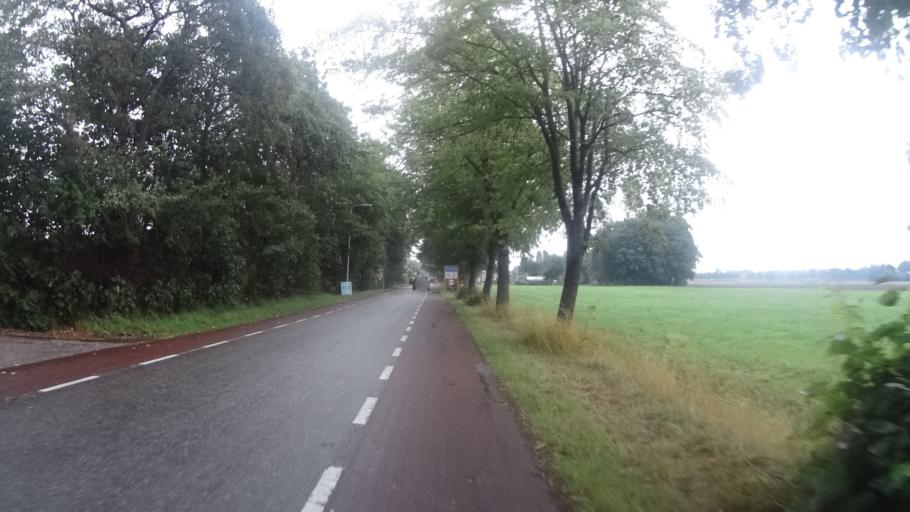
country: NL
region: Groningen
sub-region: Gemeente  Oldambt
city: Winschoten
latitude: 53.1818
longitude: 6.9530
